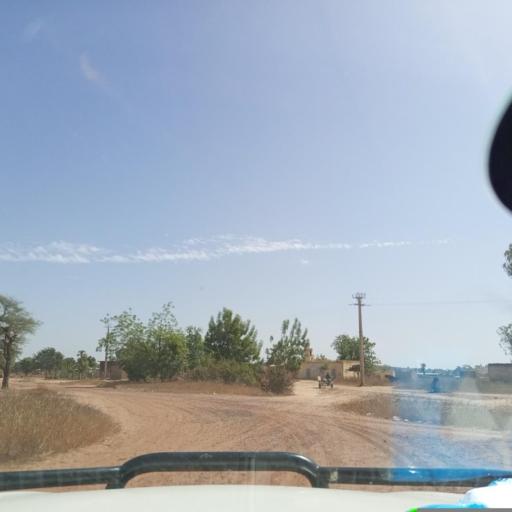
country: ML
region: Koulikoro
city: Dioila
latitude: 12.5216
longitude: -6.8102
